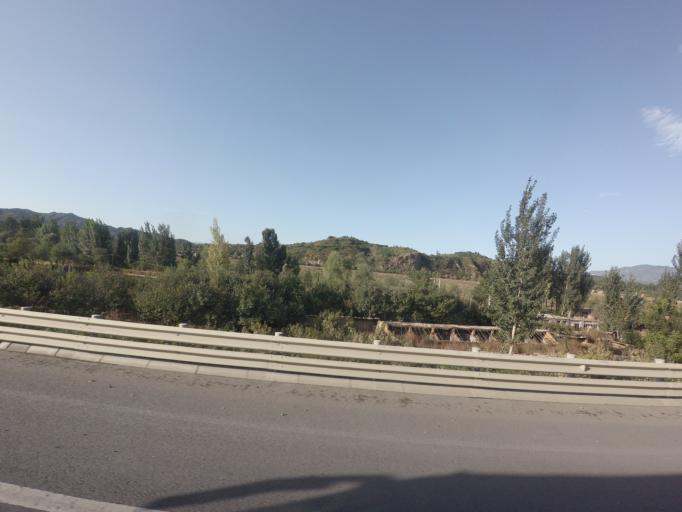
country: CN
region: Beijing
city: Jugezhuang
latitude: 40.3954
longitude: 116.9415
